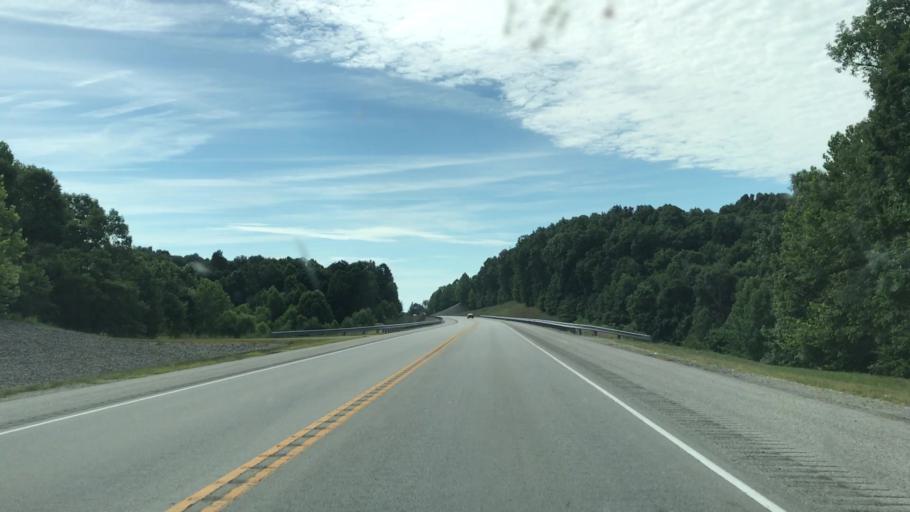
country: US
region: Kentucky
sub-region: Edmonson County
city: Brownsville
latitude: 37.1816
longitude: -86.2456
